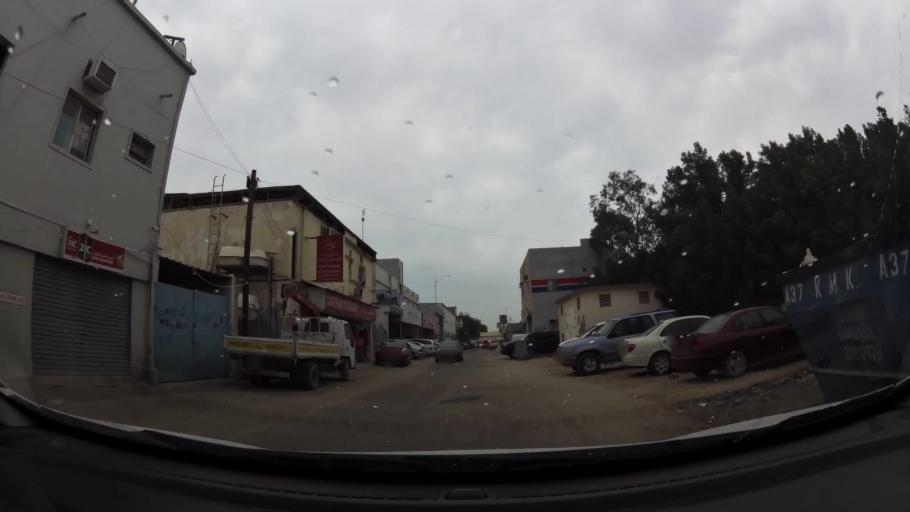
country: BH
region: Northern
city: Madinat `Isa
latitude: 26.1856
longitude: 50.5331
